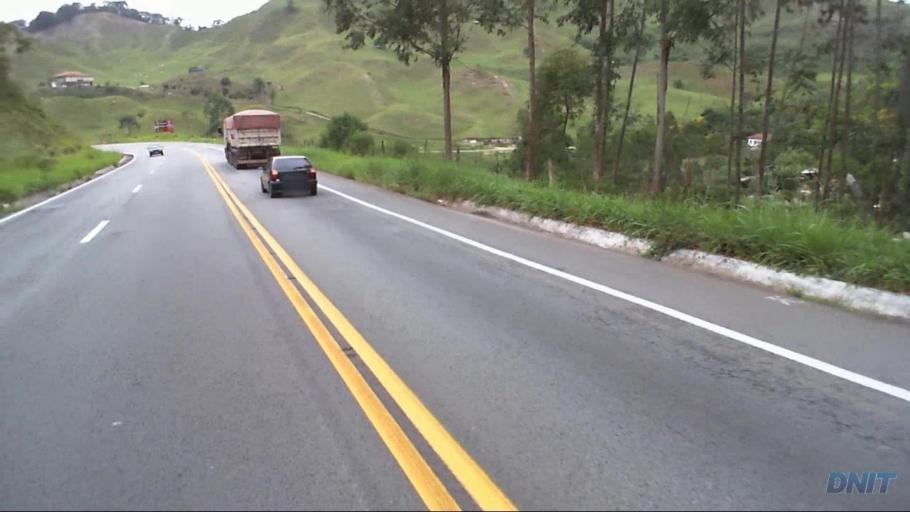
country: BR
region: Minas Gerais
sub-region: Nova Era
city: Nova Era
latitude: -19.6308
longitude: -42.8764
